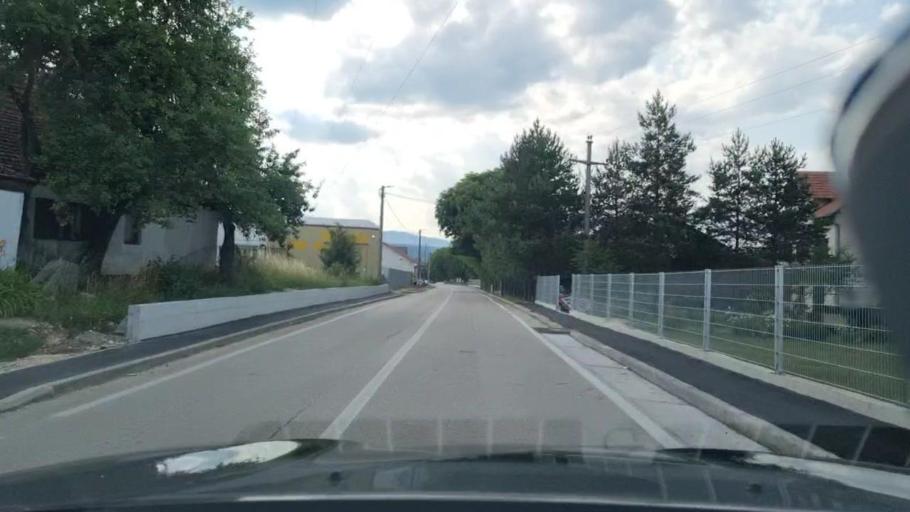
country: BA
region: Federation of Bosnia and Herzegovina
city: Glamoc
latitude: 44.0477
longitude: 16.8557
